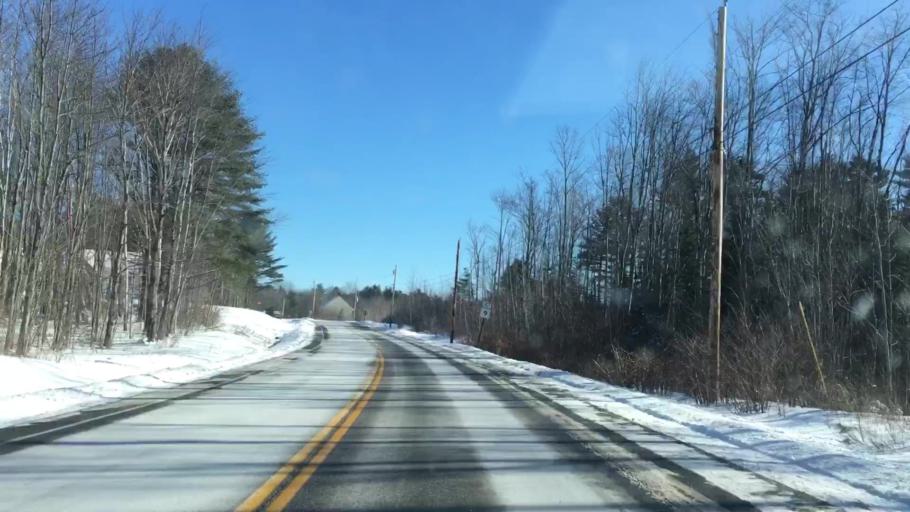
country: US
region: Maine
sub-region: Androscoggin County
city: Lisbon Falls
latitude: 44.0249
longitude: -70.0708
